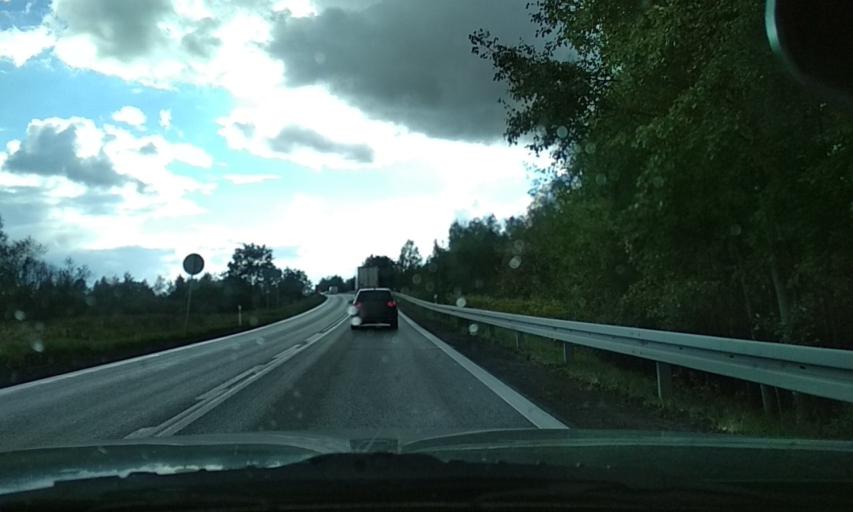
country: PL
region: Silesian Voivodeship
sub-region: Powiat gliwicki
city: Zernica
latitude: 50.2280
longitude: 18.6197
